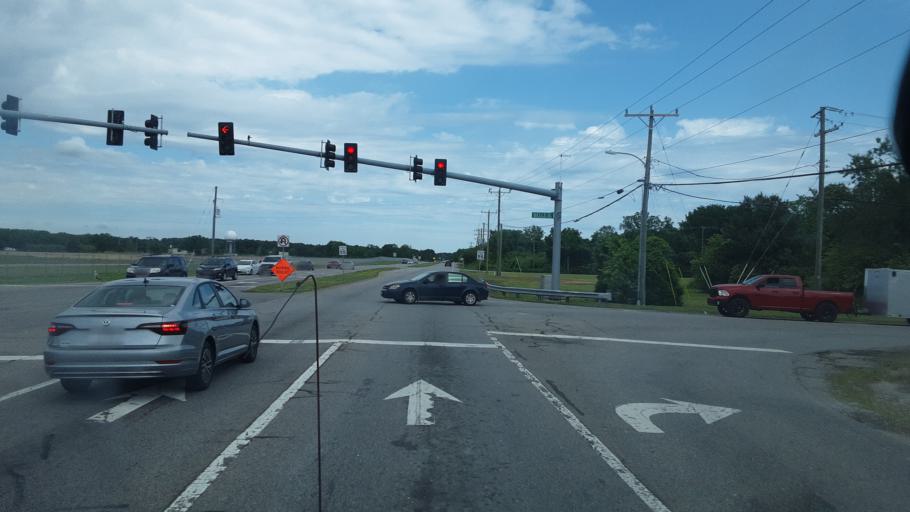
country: US
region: Virginia
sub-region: City of Virginia Beach
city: Virginia Beach
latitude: 36.8188
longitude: -76.0076
